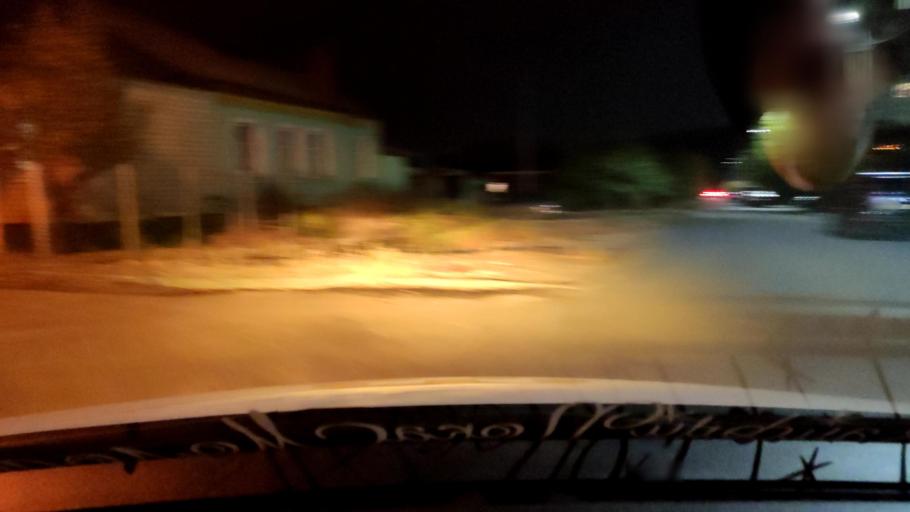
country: RU
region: Voronezj
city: Pridonskoy
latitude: 51.6594
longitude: 39.1204
